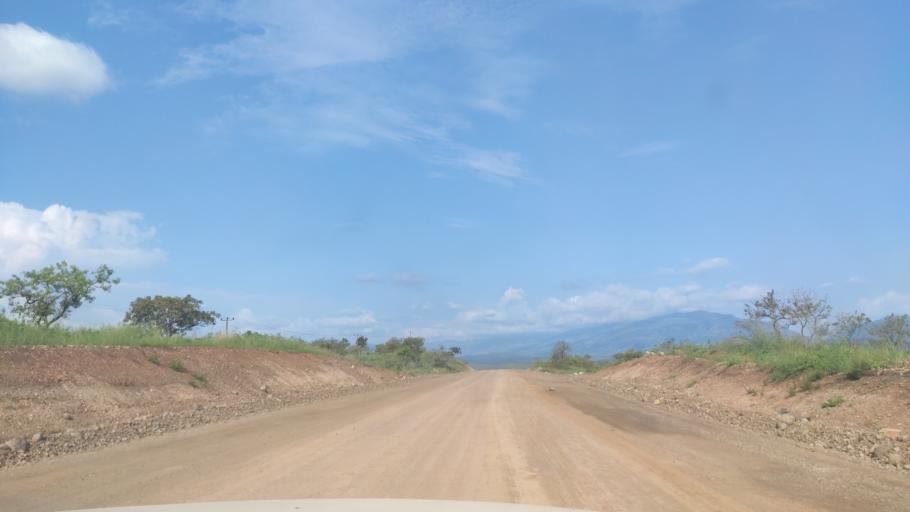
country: ET
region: Southern Nations, Nationalities, and People's Region
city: Felege Neway
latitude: 6.4248
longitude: 37.2222
